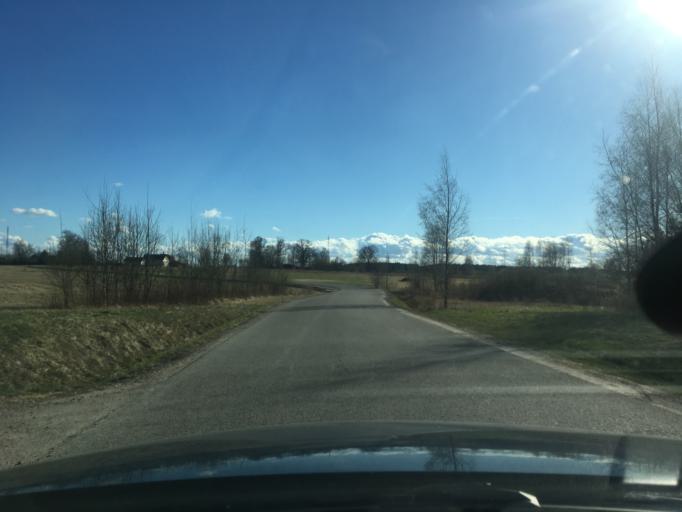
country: LV
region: Salaspils
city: Salaspils
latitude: 56.8738
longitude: 24.3249
